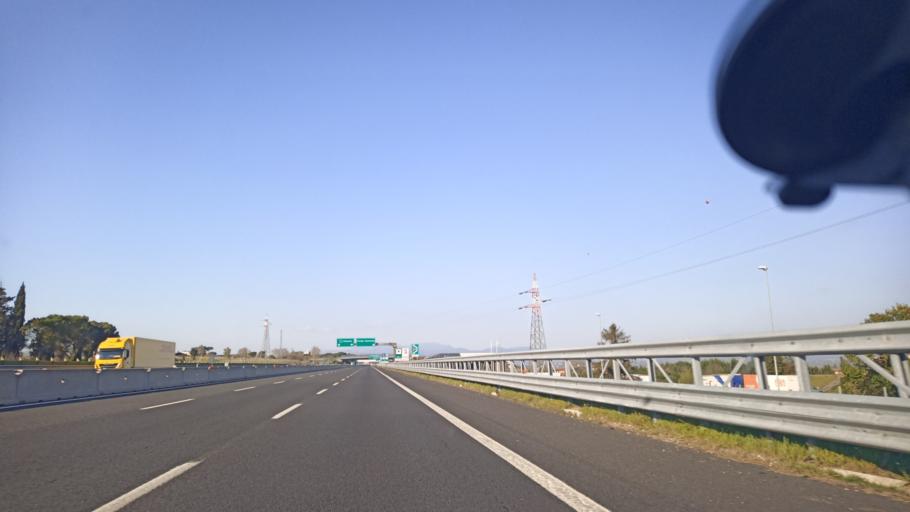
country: IT
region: Latium
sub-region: Citta metropolitana di Roma Capitale
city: Bivio di Capanelle
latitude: 42.1232
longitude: 12.5958
